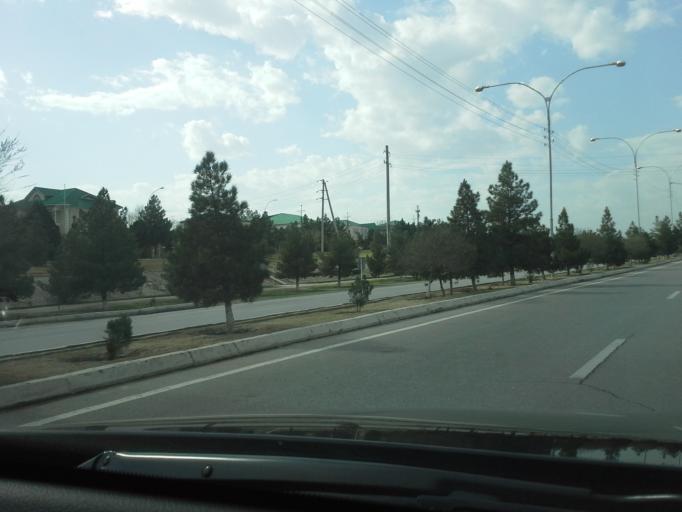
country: TM
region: Ahal
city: Ashgabat
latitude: 37.9592
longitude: 58.3183
